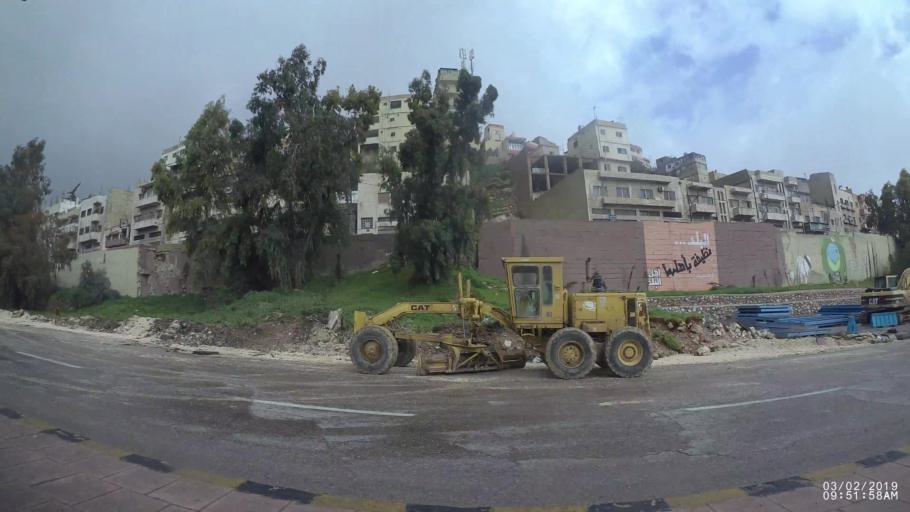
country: JO
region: Amman
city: Amman
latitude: 31.9455
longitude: 35.9216
